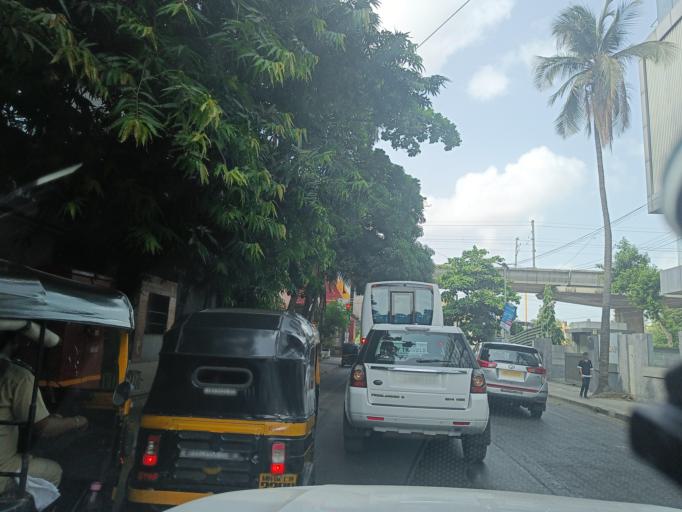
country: IN
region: Maharashtra
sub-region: Mumbai Suburban
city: Powai
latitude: 19.1130
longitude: 72.8670
